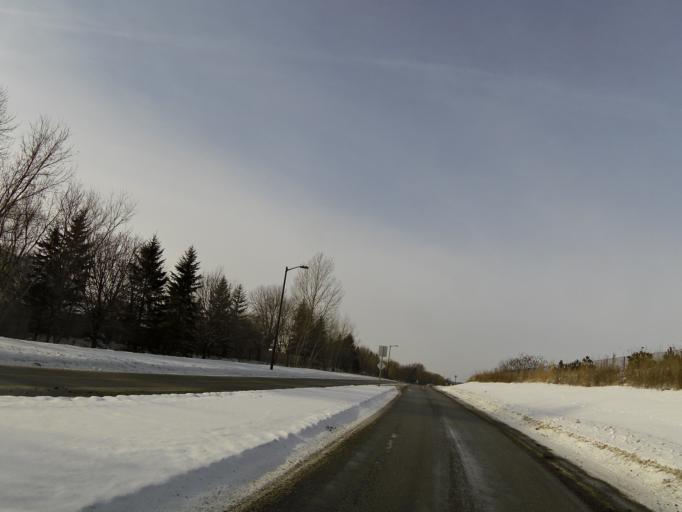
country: US
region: Minnesota
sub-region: Hennepin County
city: Eden Prairie
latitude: 44.8496
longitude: -93.4868
